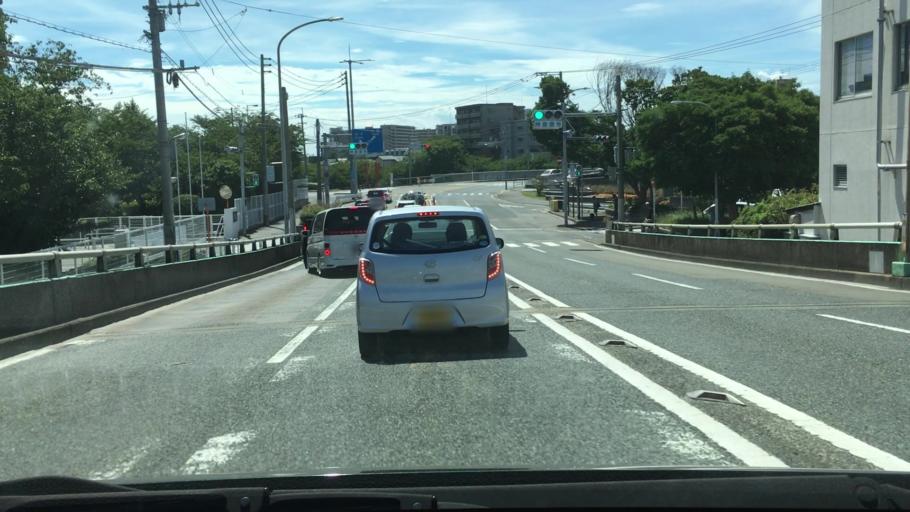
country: JP
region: Fukuoka
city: Fukuoka-shi
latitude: 33.5757
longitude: 130.4211
